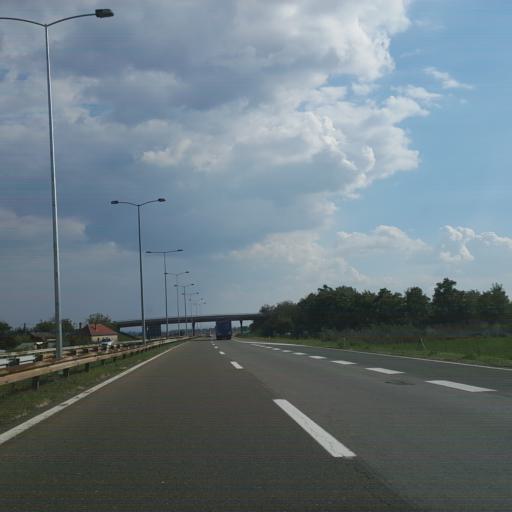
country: RS
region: Central Serbia
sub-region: Podunavski Okrug
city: Velika Plana
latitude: 44.3375
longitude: 21.0848
